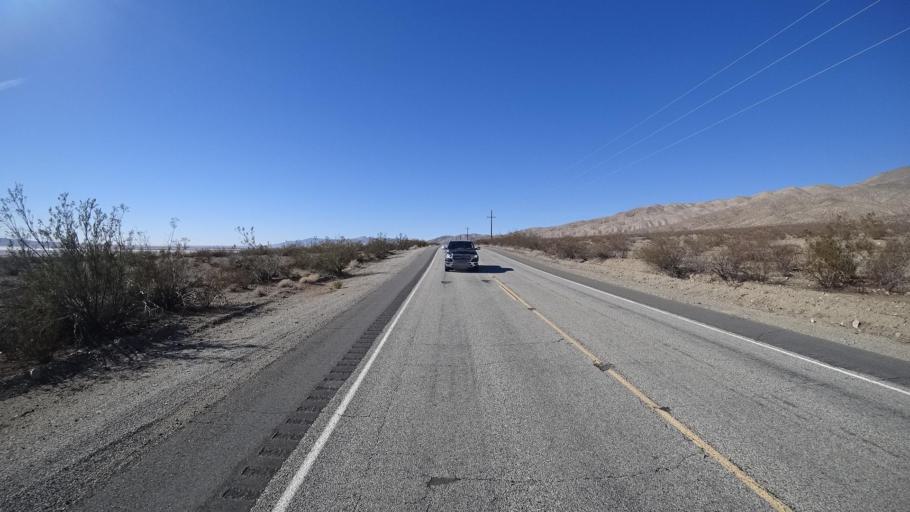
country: US
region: California
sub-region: Kern County
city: Inyokern
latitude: 35.3783
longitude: -117.8620
